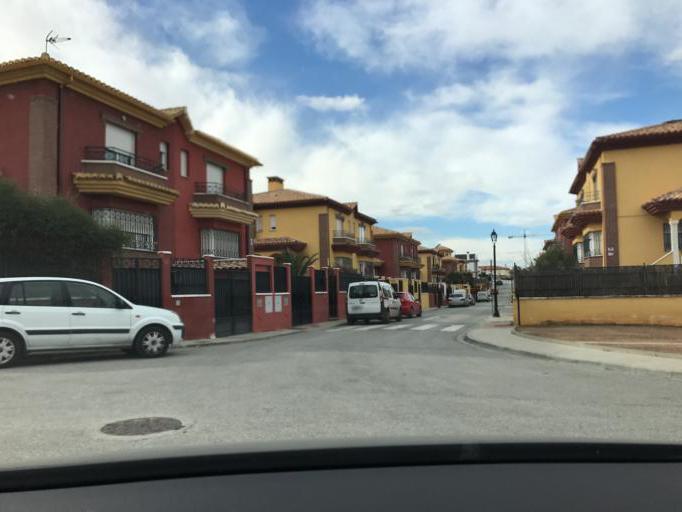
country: ES
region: Andalusia
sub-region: Provincia de Granada
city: Alhendin
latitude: 37.1056
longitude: -3.6582
